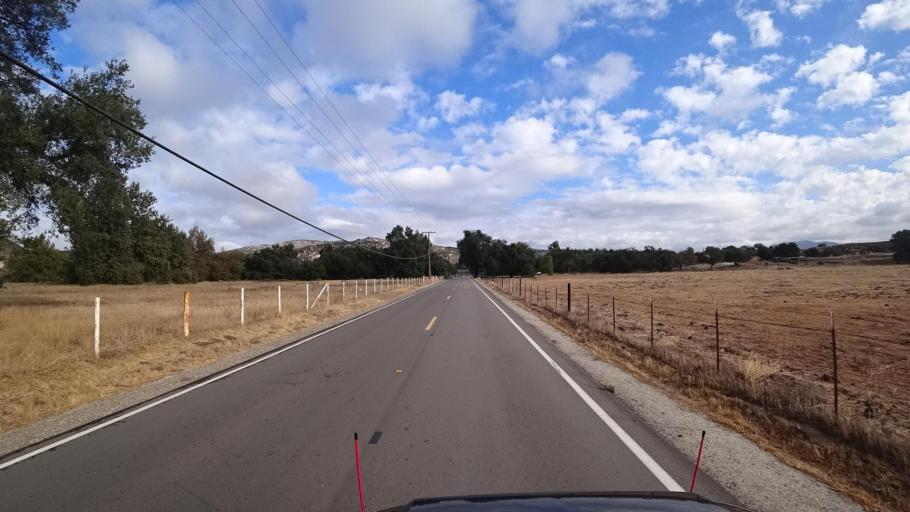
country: MX
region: Baja California
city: Tecate
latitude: 32.6195
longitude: -116.6134
